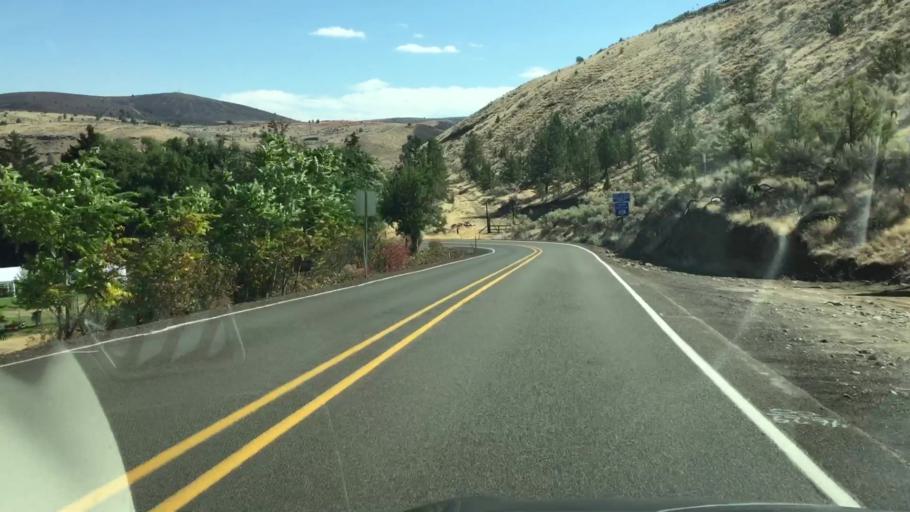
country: US
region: Oregon
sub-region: Wasco County
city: The Dalles
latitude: 45.1684
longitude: -121.0823
